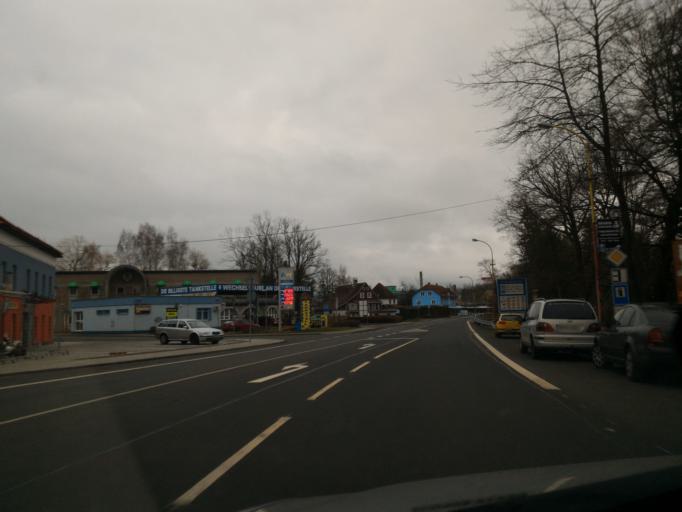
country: CZ
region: Ustecky
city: Varnsdorf
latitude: 50.9210
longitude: 14.6075
